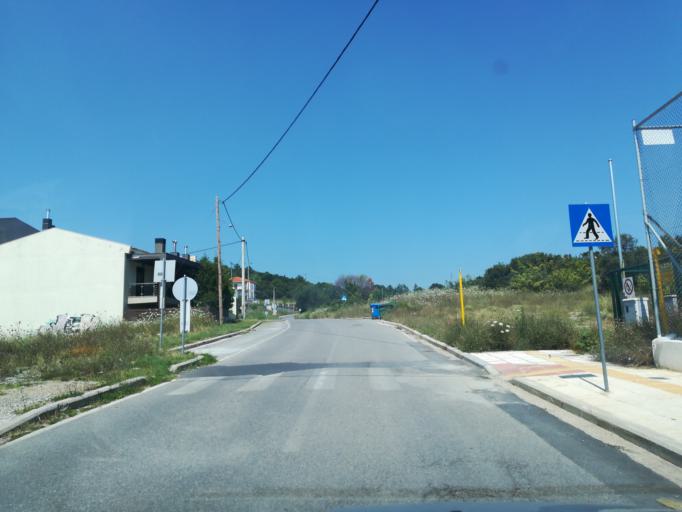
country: GR
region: Central Macedonia
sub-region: Nomos Thessalonikis
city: Asvestochori
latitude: 40.6291
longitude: 23.0378
